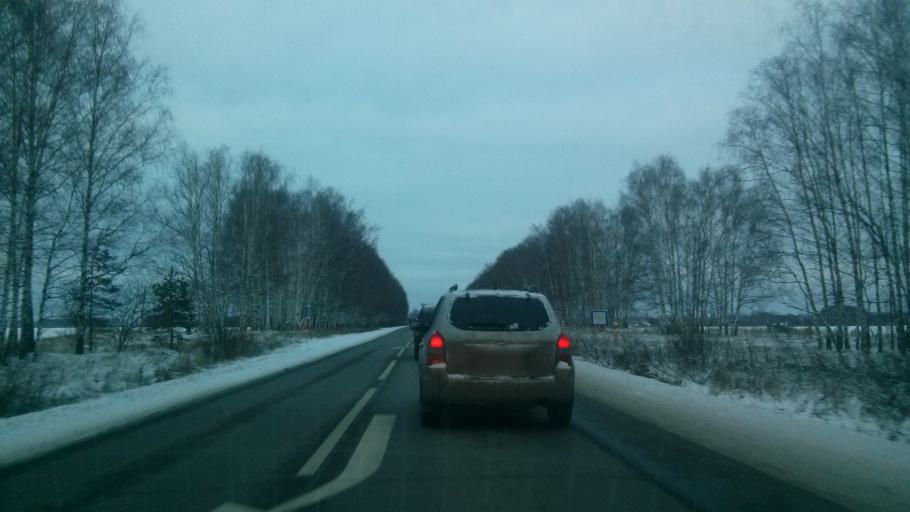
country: RU
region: Nizjnij Novgorod
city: Vorsma
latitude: 56.0275
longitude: 43.3588
